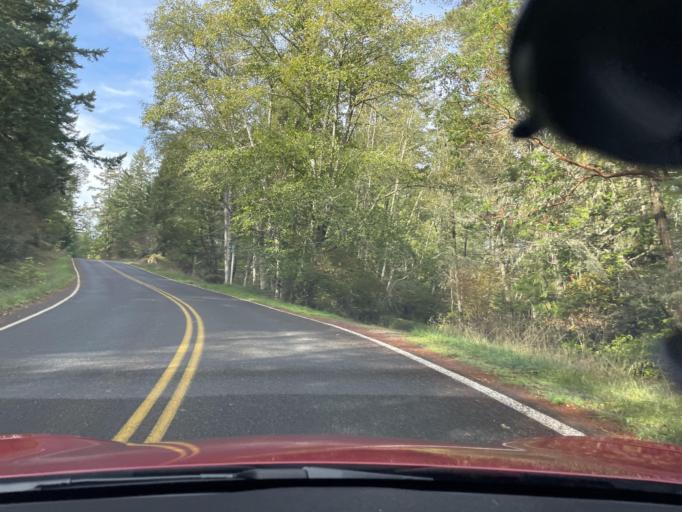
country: US
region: Washington
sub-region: San Juan County
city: Friday Harbor
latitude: 48.5258
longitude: -122.9745
